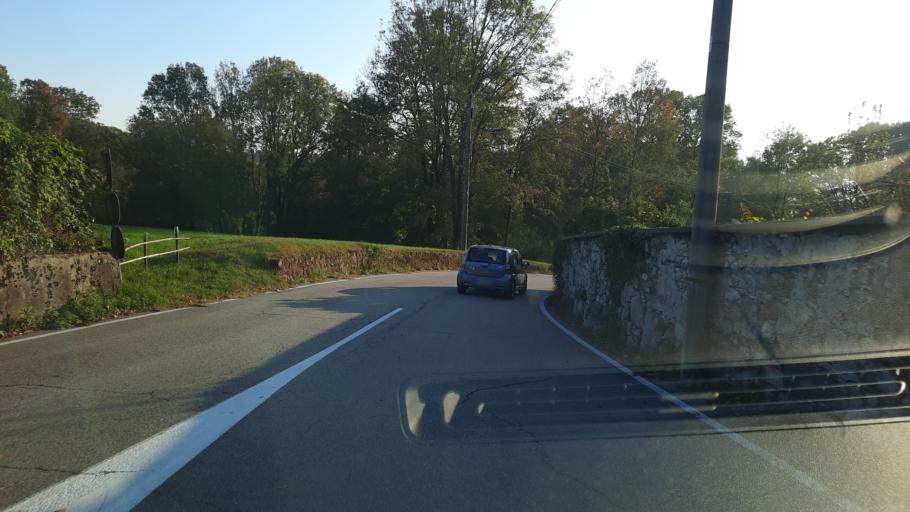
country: IT
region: Piedmont
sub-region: Provincia di Novara
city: Ameno
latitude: 45.7865
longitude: 8.4357
